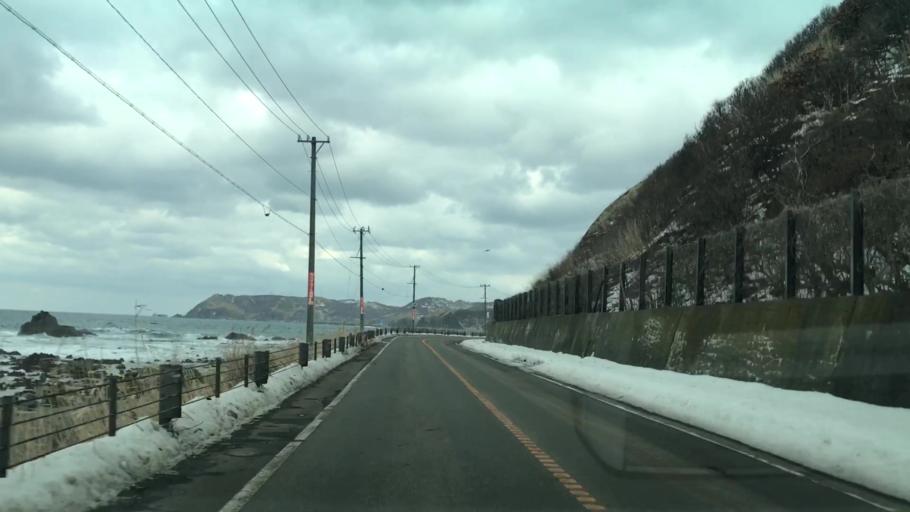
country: JP
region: Hokkaido
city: Yoichi
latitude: 43.3366
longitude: 140.4479
